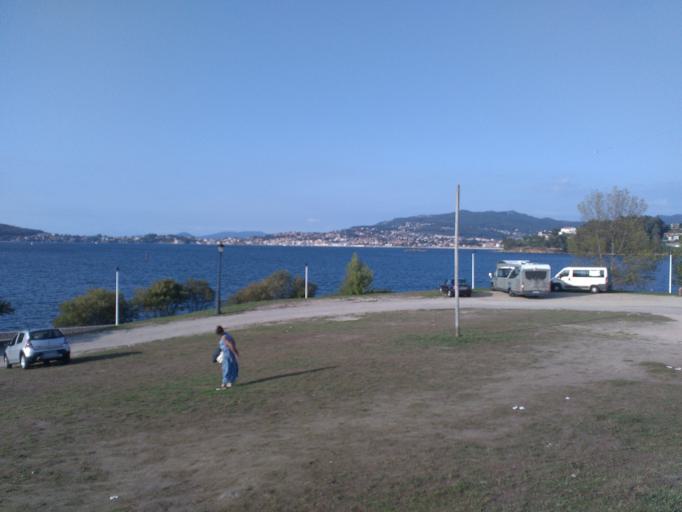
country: ES
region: Galicia
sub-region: Provincia de Pontevedra
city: Baiona
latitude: 42.1150
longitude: -8.8368
